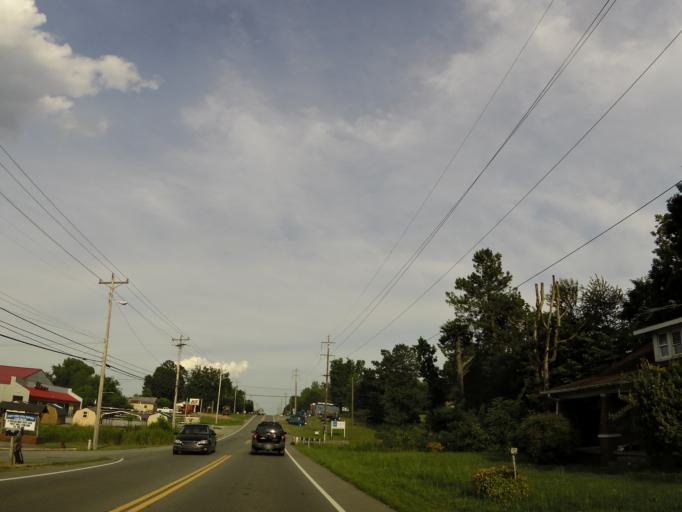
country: US
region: Tennessee
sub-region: Humphreys County
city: McEwen
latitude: 36.1064
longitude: -87.6296
